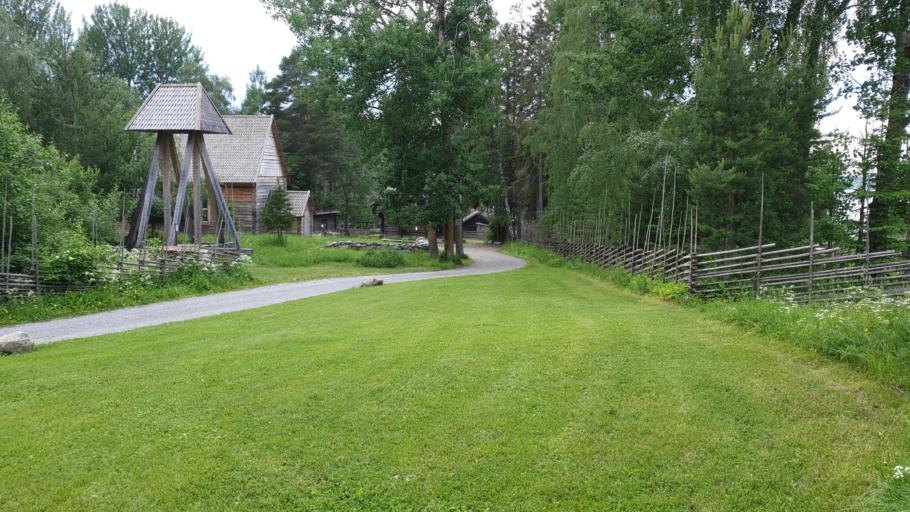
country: SE
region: Jaemtland
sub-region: OEstersunds Kommun
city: Ostersund
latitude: 63.1892
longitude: 14.6355
